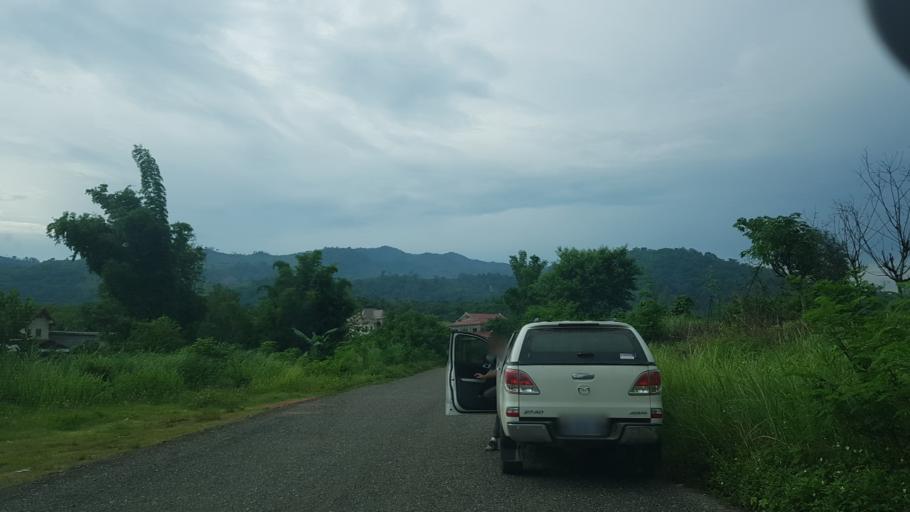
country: LA
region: Oudomxai
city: Muang Xay
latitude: 20.6960
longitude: 101.9899
